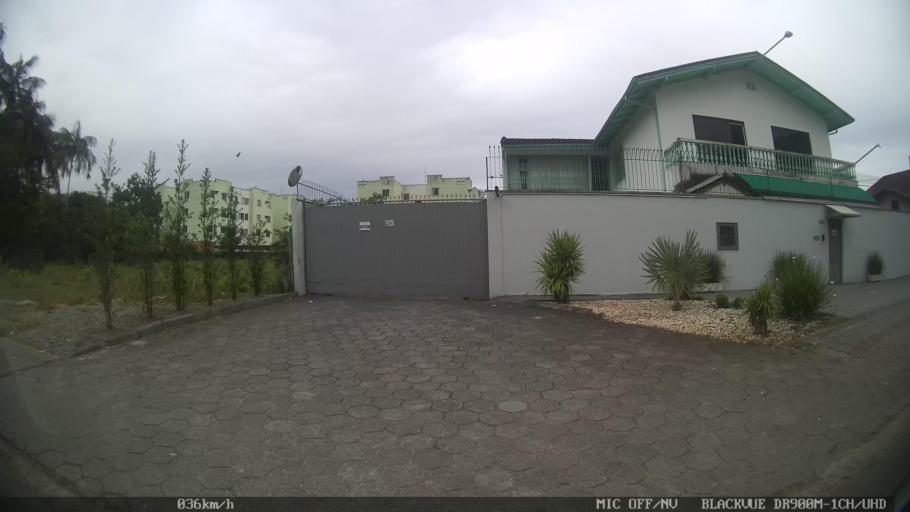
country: BR
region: Santa Catarina
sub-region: Joinville
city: Joinville
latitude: -26.2656
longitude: -48.8252
